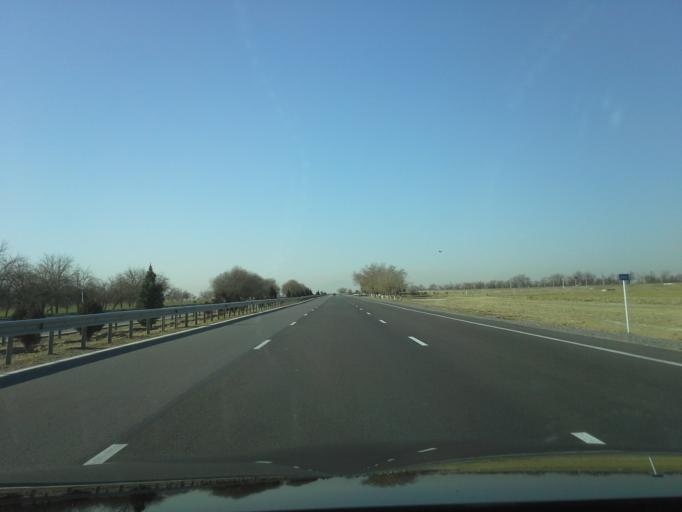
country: TM
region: Ahal
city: Annau
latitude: 37.8997
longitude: 58.5805
